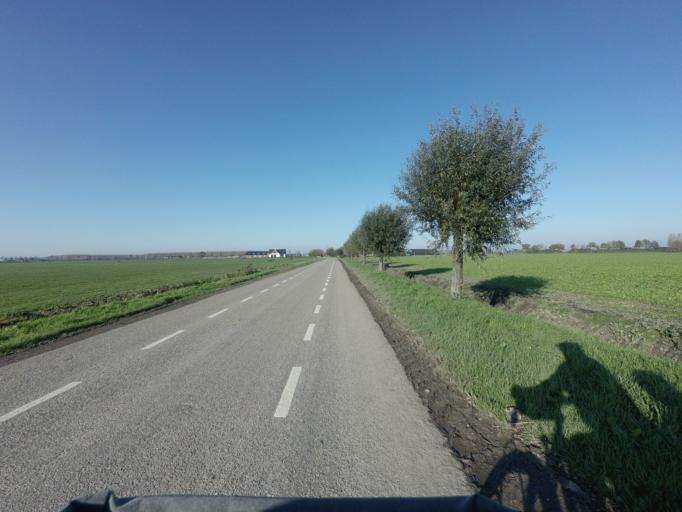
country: NL
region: North Brabant
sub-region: Gemeente Waalwijk
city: Waalwijk
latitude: 51.7484
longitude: 5.0591
